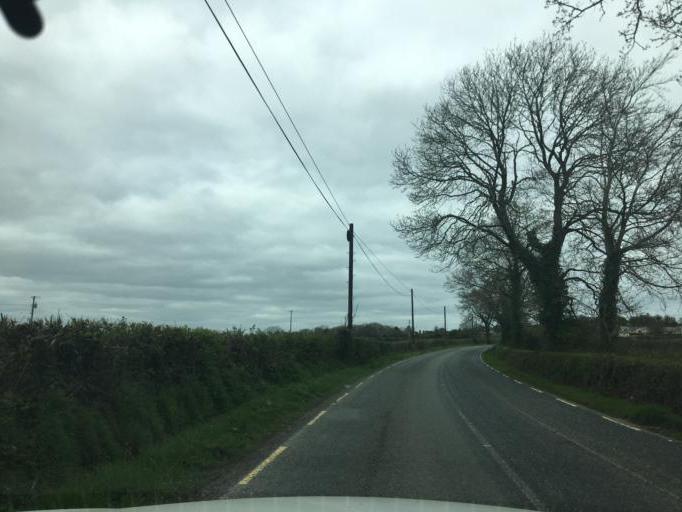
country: IE
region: Leinster
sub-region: Loch Garman
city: New Ross
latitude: 52.4349
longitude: -6.9650
